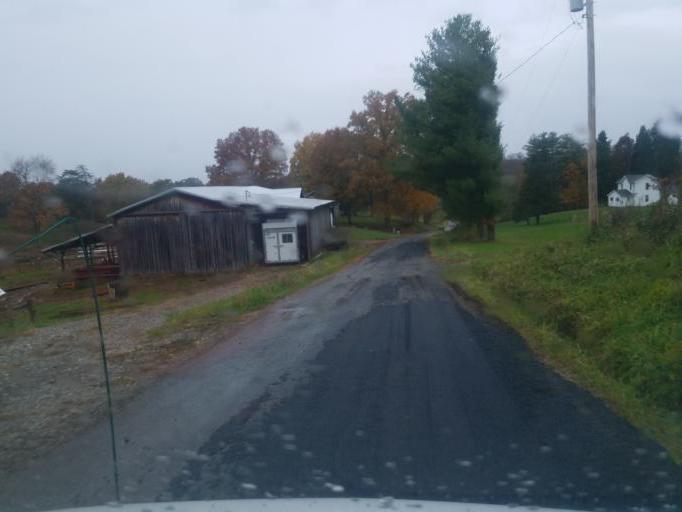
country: US
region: West Virginia
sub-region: Wood County
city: Blennerhassett
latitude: 39.3232
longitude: -81.6128
